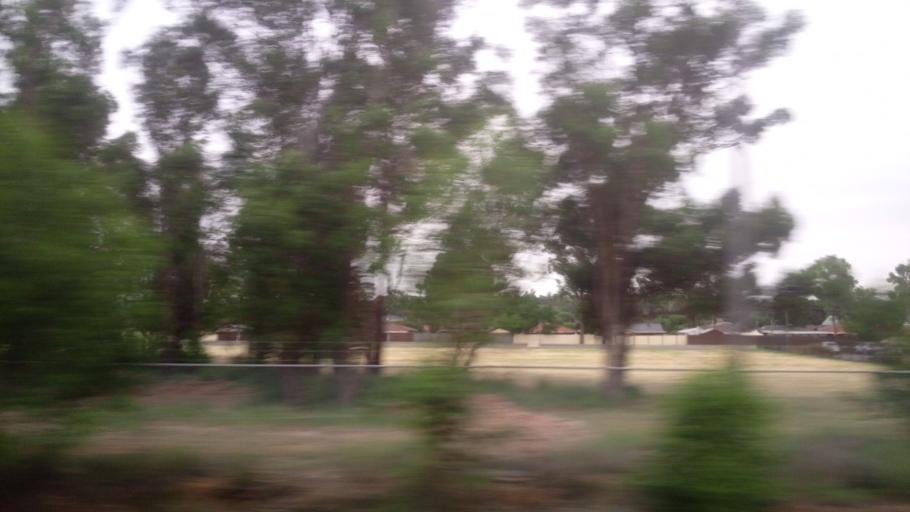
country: AU
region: New South Wales
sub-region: Penrith Municipality
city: Werrington County
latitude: -33.7576
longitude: 150.7483
